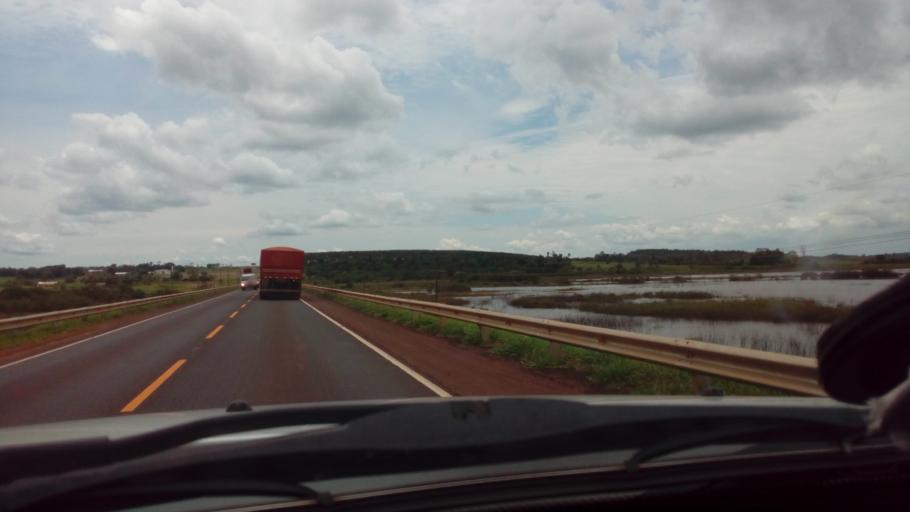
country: PY
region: Alto Parana
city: Colonia Yguazu
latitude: -25.6117
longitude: -54.9448
